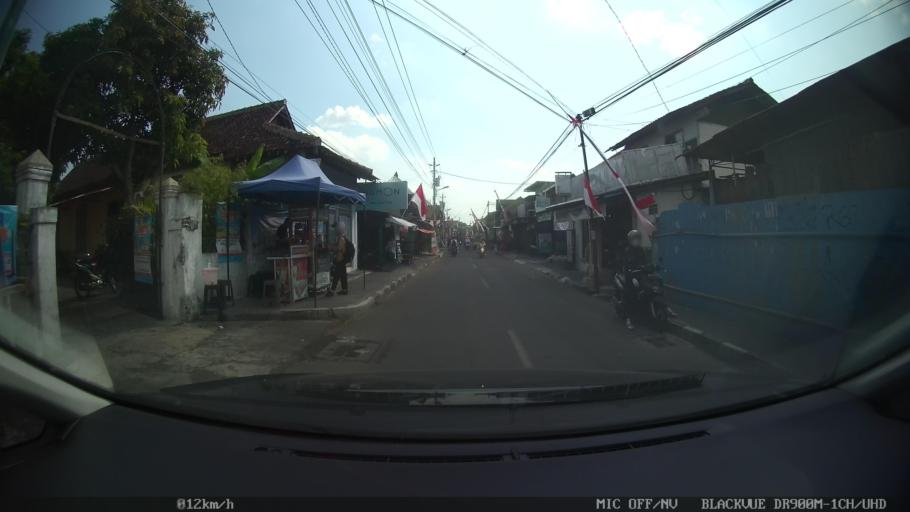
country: ID
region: Daerah Istimewa Yogyakarta
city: Yogyakarta
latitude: -7.8274
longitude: 110.3969
